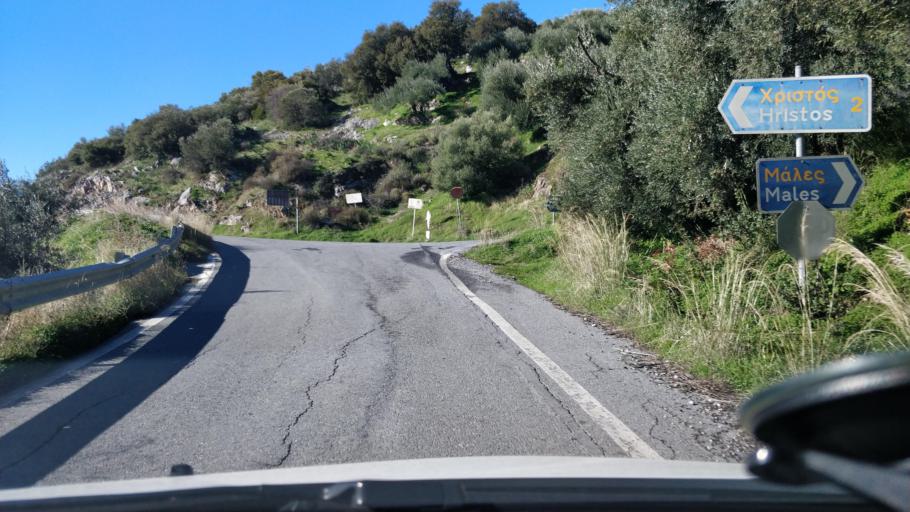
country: GR
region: Crete
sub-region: Nomos Lasithiou
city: Kritsa
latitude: 35.0793
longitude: 25.5810
